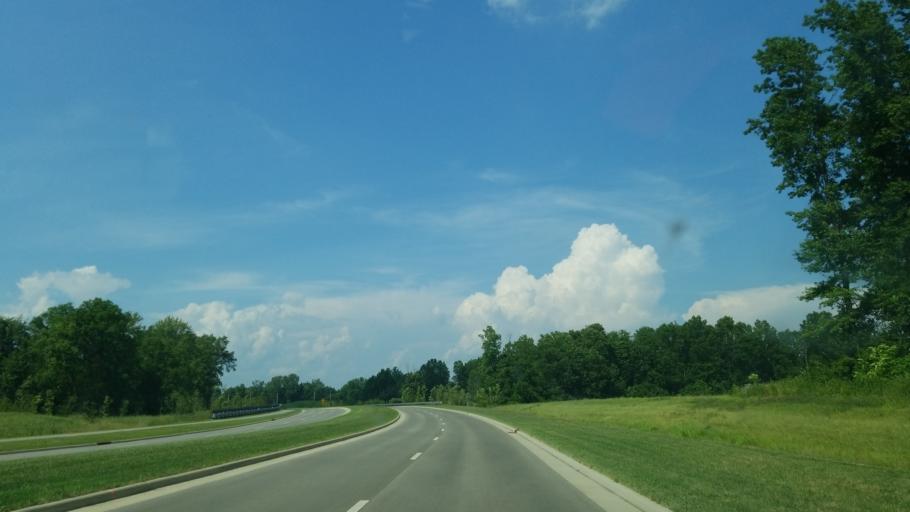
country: US
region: Ohio
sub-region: Delaware County
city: Delaware
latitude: 40.2490
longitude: -83.0924
